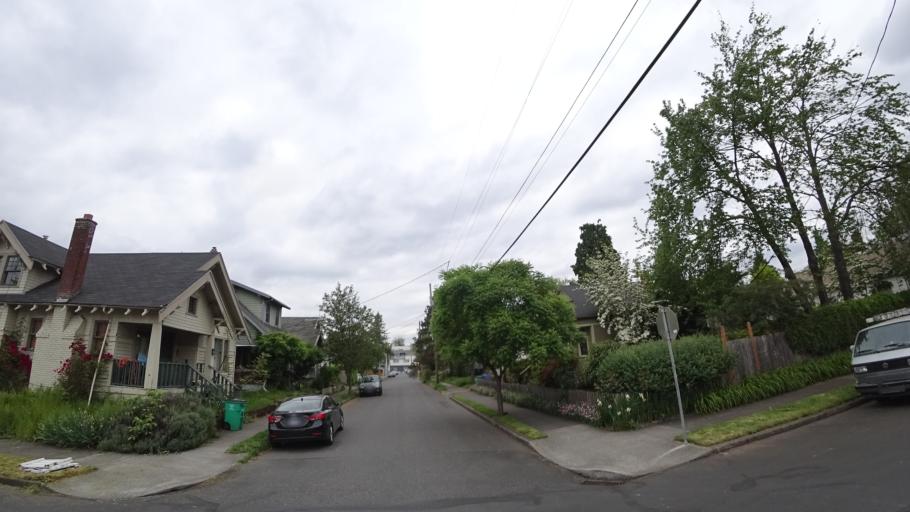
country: US
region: Oregon
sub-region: Multnomah County
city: Portland
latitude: 45.5150
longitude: -122.6171
